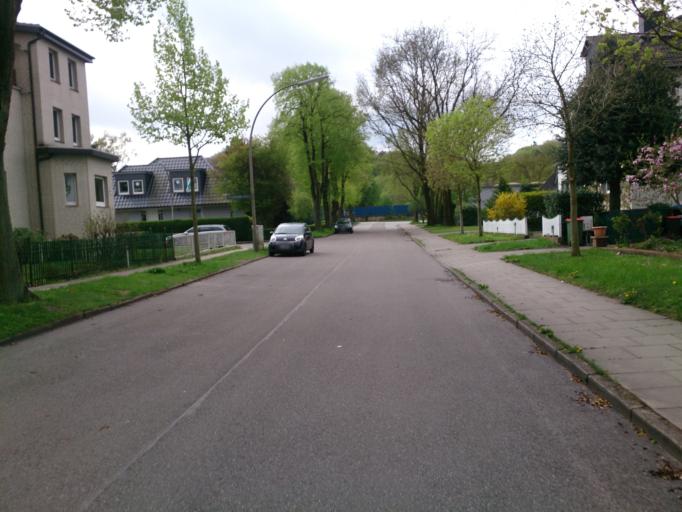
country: DE
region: Hamburg
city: Harburg
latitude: 53.4735
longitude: 9.9035
